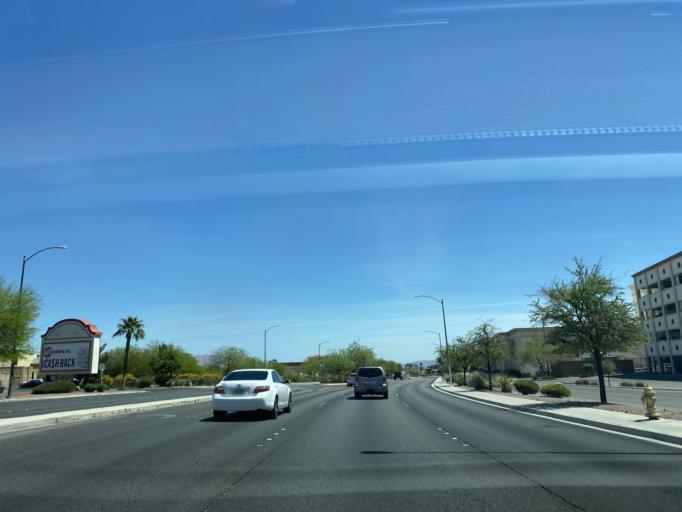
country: US
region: Nevada
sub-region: Clark County
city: Las Vegas
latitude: 36.2000
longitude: -115.1937
